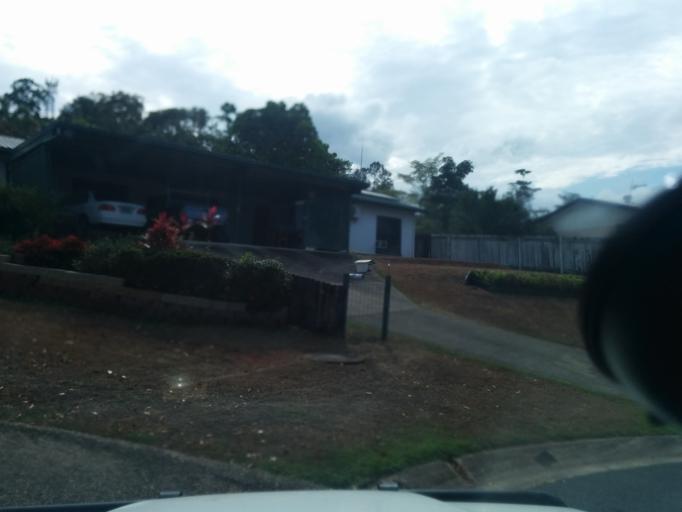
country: AU
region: Queensland
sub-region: Cairns
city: Woree
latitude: -16.9527
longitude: 145.7370
